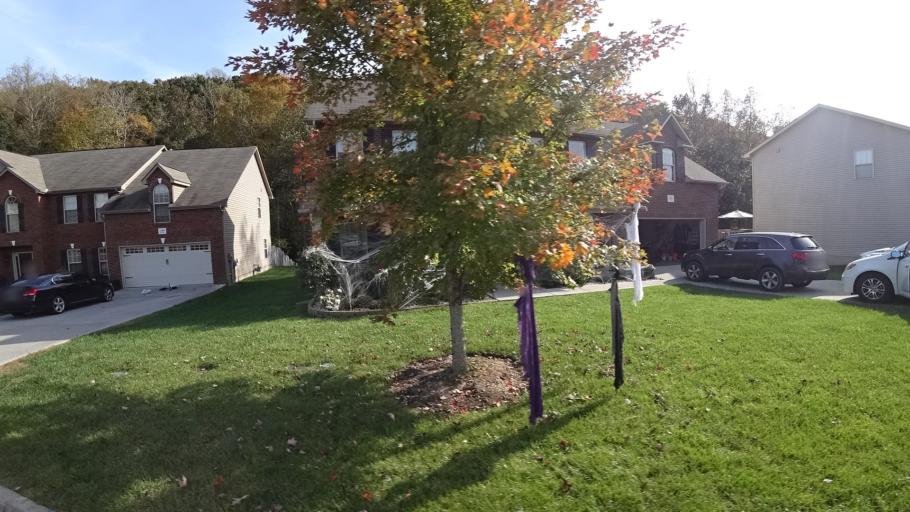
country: US
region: Tennessee
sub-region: Knox County
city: Farragut
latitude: 35.9117
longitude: -84.1830
